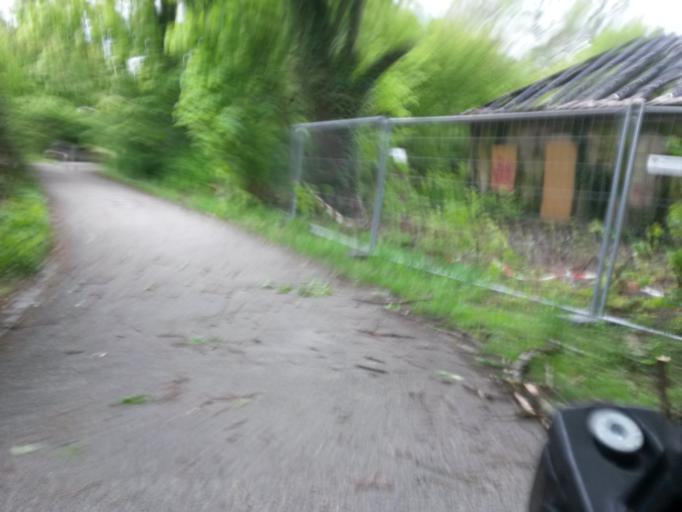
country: DE
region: Baden-Wuerttemberg
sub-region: Tuebingen Region
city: Bad Waldsee
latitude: 47.9204
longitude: 9.7501
